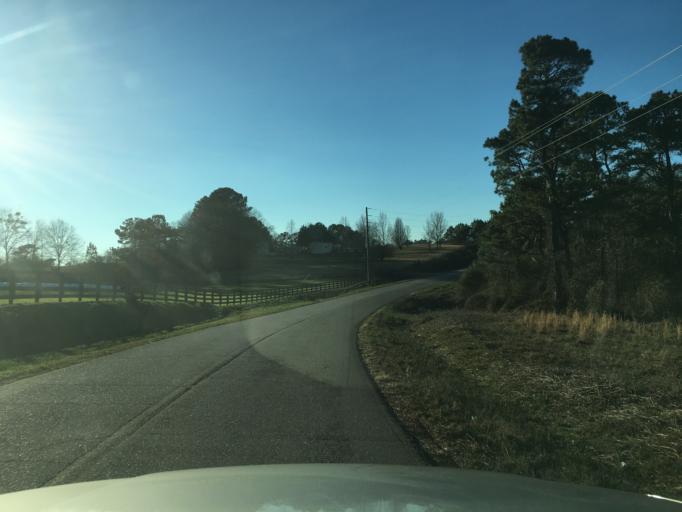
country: US
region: Georgia
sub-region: Carroll County
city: Carrollton
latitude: 33.4395
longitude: -85.1271
